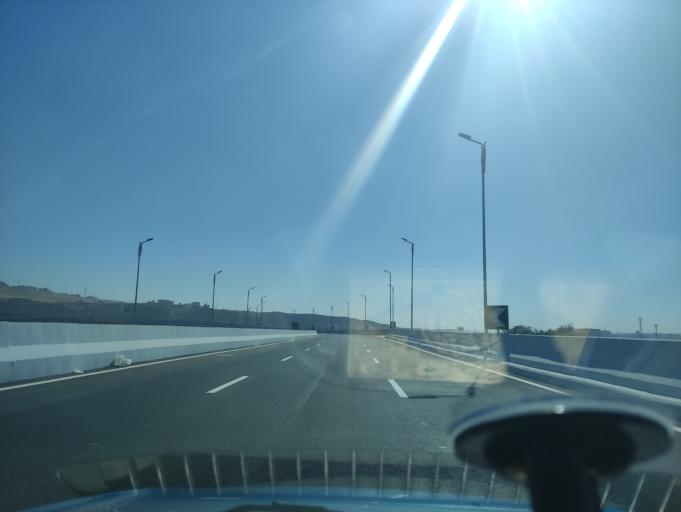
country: EG
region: Al Jizah
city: Al Jizah
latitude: 30.0069
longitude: 31.2620
